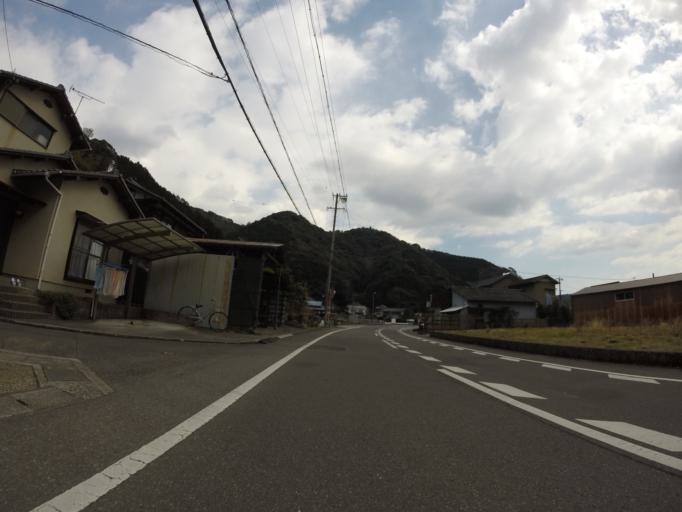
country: JP
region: Shizuoka
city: Shizuoka-shi
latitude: 35.0528
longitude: 138.3517
